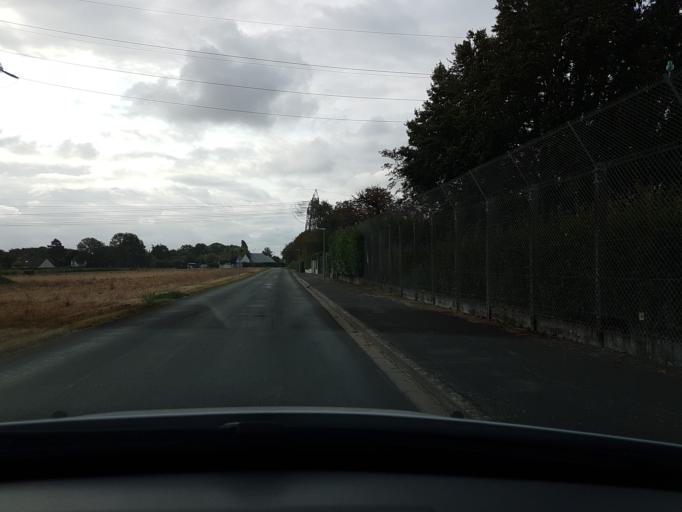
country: FR
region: Centre
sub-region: Departement d'Indre-et-Loire
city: Larcay
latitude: 47.3529
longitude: 0.7680
